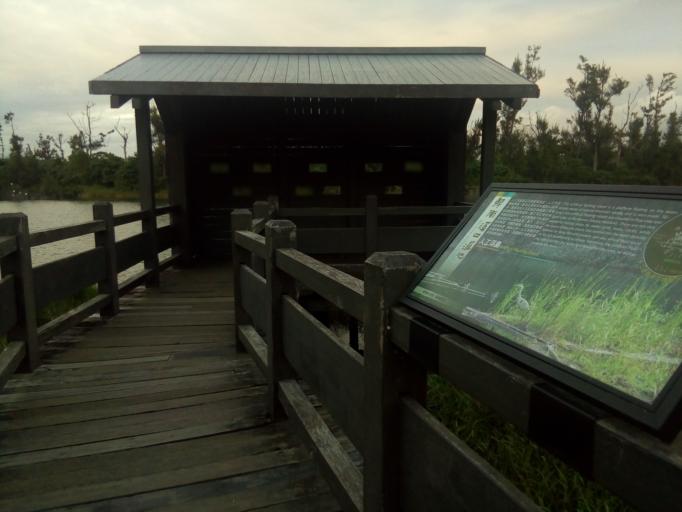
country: TW
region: Taiwan
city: Taitung City
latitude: 22.7559
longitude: 121.1660
